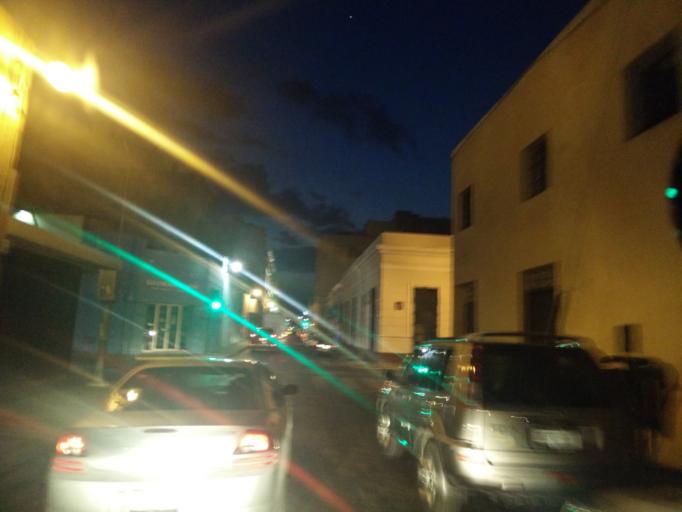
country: MX
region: Yucatan
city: Merida
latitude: 20.9696
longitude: -89.6211
